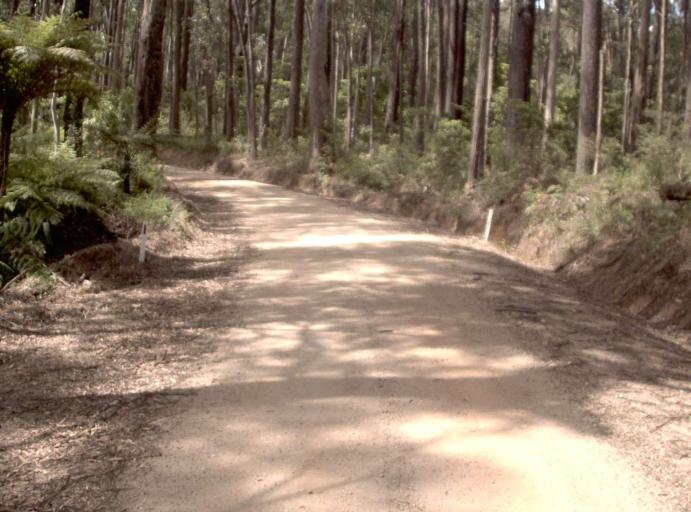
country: AU
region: Victoria
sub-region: East Gippsland
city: Lakes Entrance
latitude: -37.5900
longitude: 148.7246
